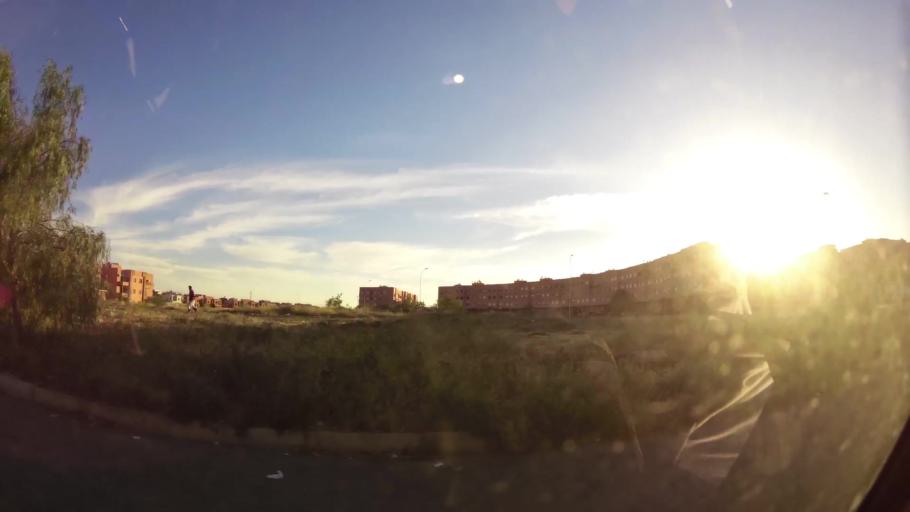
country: MA
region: Marrakech-Tensift-Al Haouz
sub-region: Marrakech
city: Marrakesh
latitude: 31.7499
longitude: -8.1099
